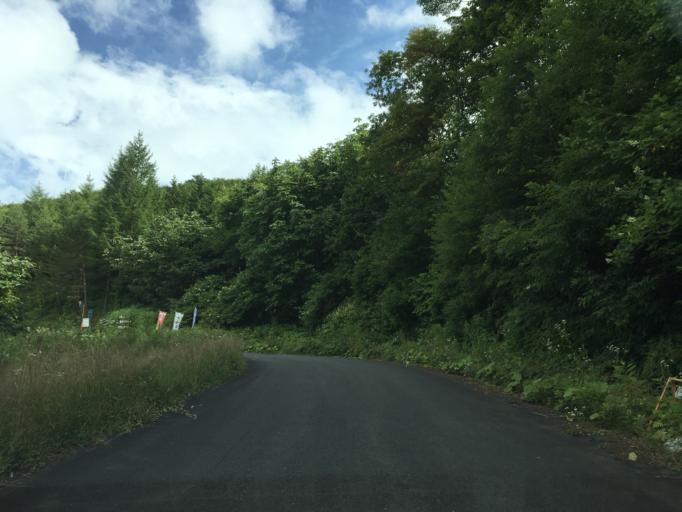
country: JP
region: Iwate
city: Ofunato
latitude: 38.9773
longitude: 141.4521
